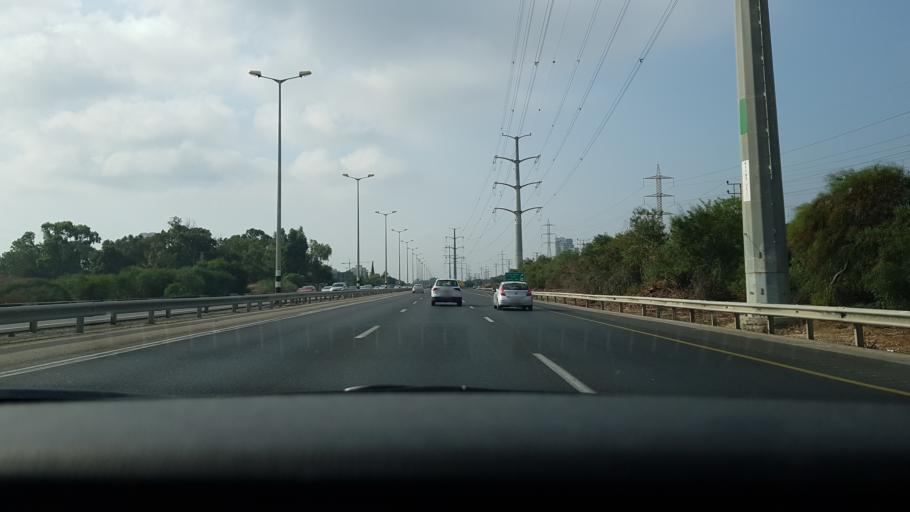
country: IL
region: Central District
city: Rishon LeZiyyon
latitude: 31.9851
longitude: 34.7956
